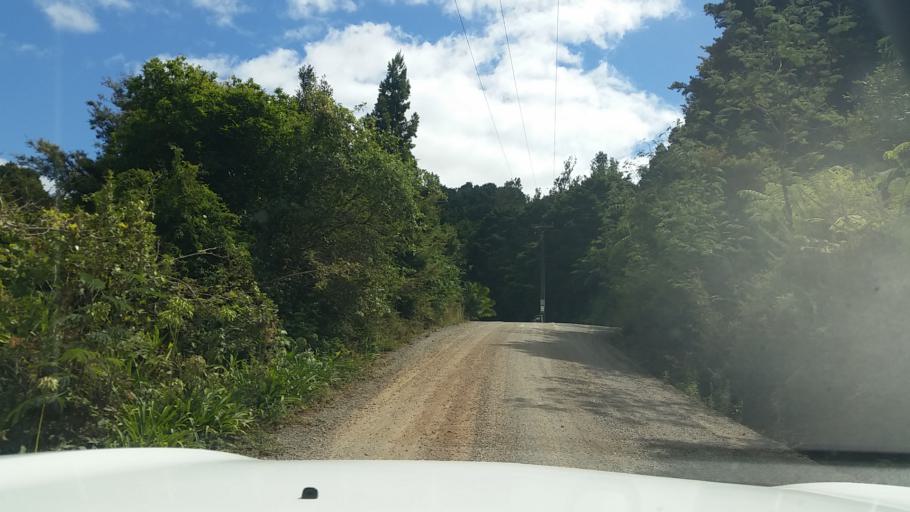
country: NZ
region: Northland
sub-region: Whangarei
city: Whangarei
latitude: -35.6628
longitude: 174.3472
